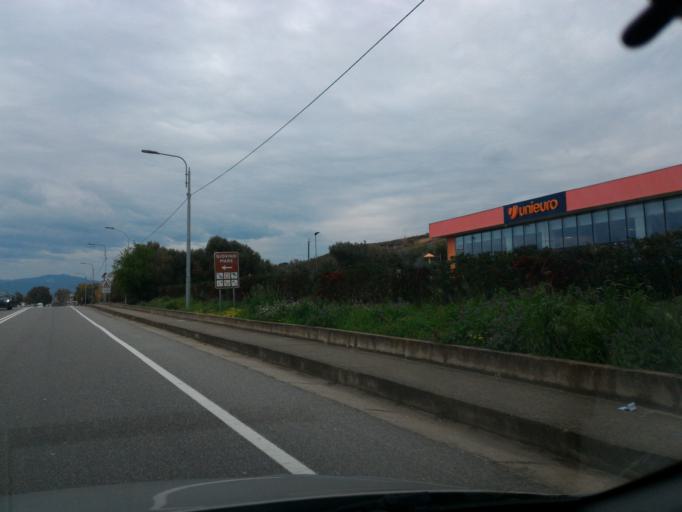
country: IT
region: Calabria
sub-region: Provincia di Catanzaro
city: Barone
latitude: 38.8379
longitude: 16.6401
